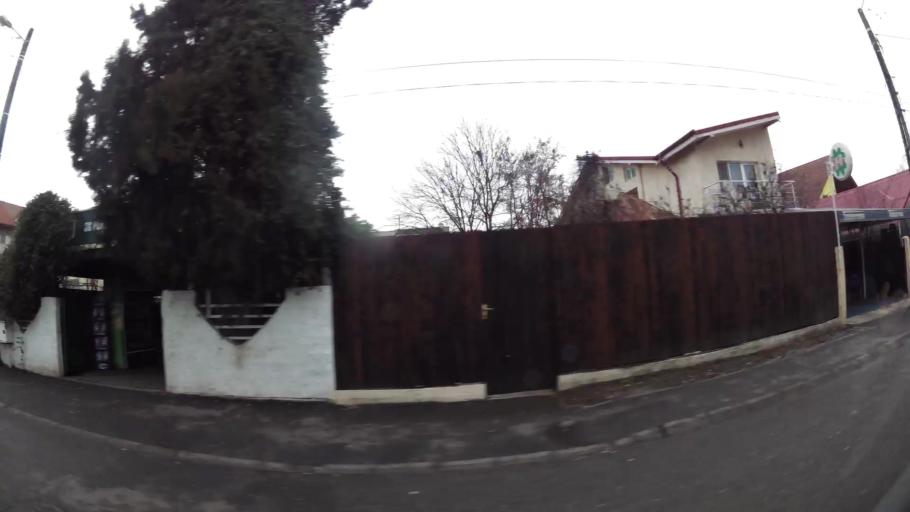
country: RO
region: Ilfov
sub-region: Comuna Otopeni
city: Otopeni
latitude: 44.5466
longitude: 26.0708
